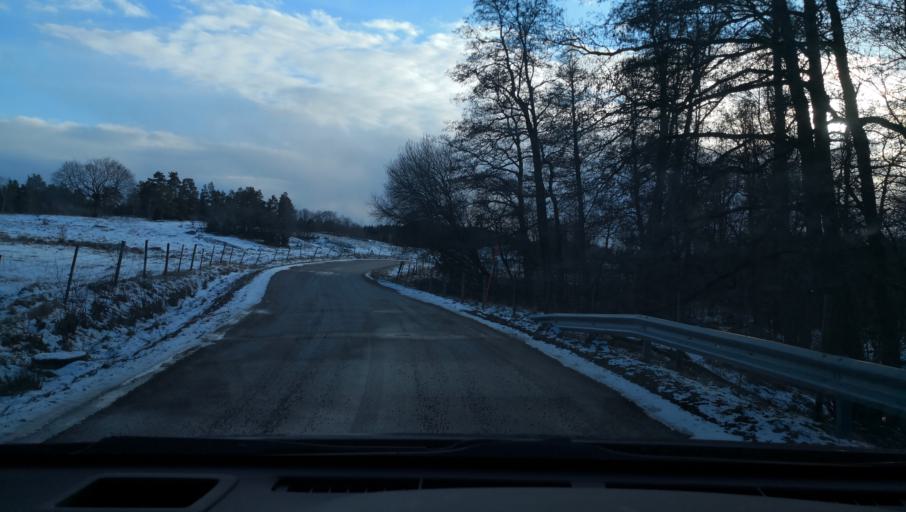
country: SE
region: Uppsala
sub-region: Enkopings Kommun
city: Irsta
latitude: 59.6591
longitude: 16.7851
